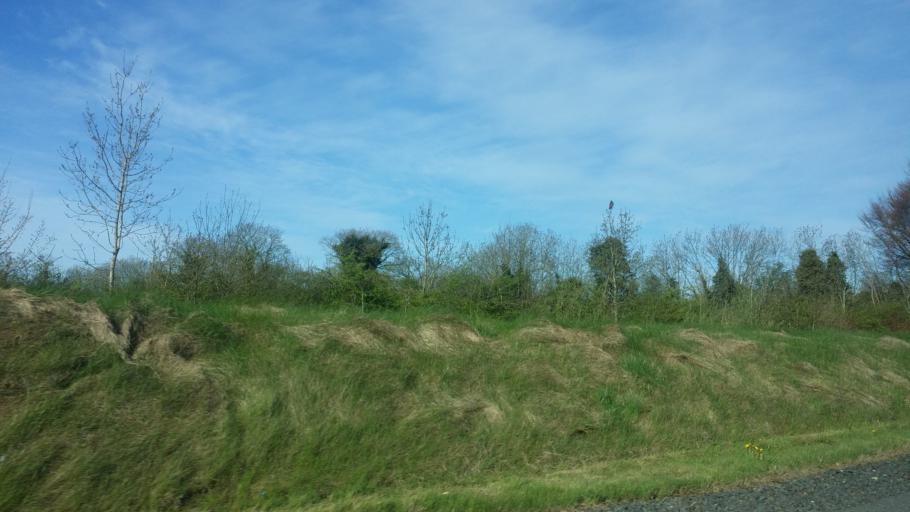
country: IE
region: Leinster
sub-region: An Mhi
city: Navan
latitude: 53.6692
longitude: -6.7659
